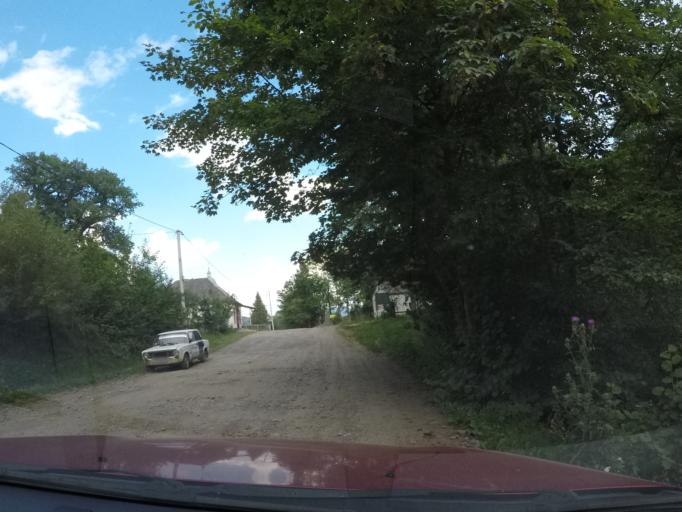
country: UA
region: Zakarpattia
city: Velykyi Bereznyi
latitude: 49.0290
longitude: 22.5905
